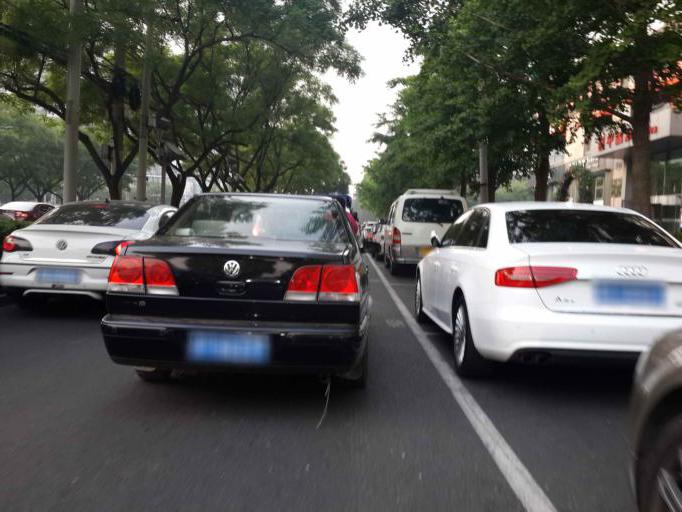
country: CN
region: Beijing
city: Chaowai
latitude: 39.9312
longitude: 116.4444
